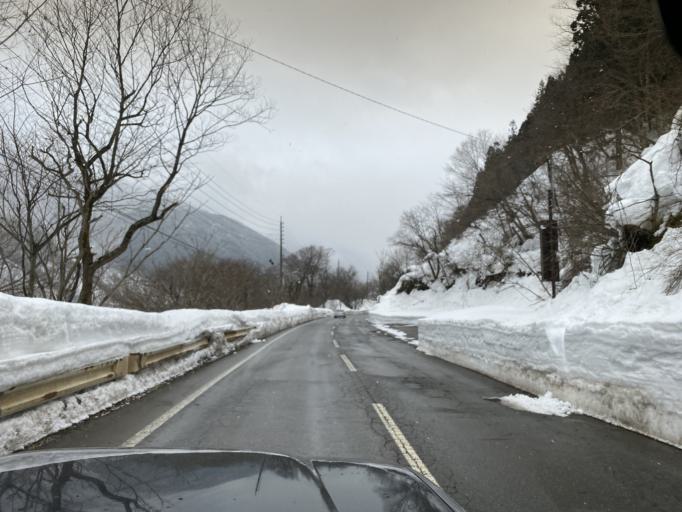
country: JP
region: Toyama
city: Fukumitsu
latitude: 36.2159
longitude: 136.8856
